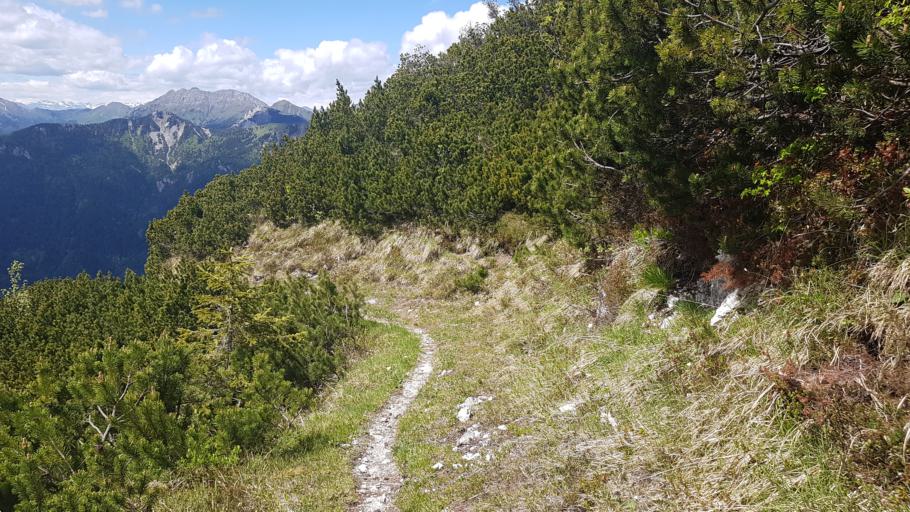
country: IT
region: Friuli Venezia Giulia
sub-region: Provincia di Udine
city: Moggio Udinese
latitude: 46.4781
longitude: 13.2171
